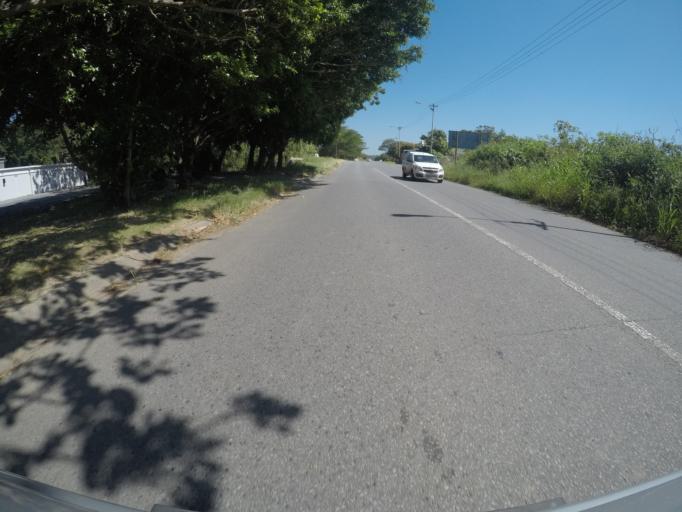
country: ZA
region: Eastern Cape
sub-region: Buffalo City Metropolitan Municipality
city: East London
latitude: -32.9724
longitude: 27.9236
